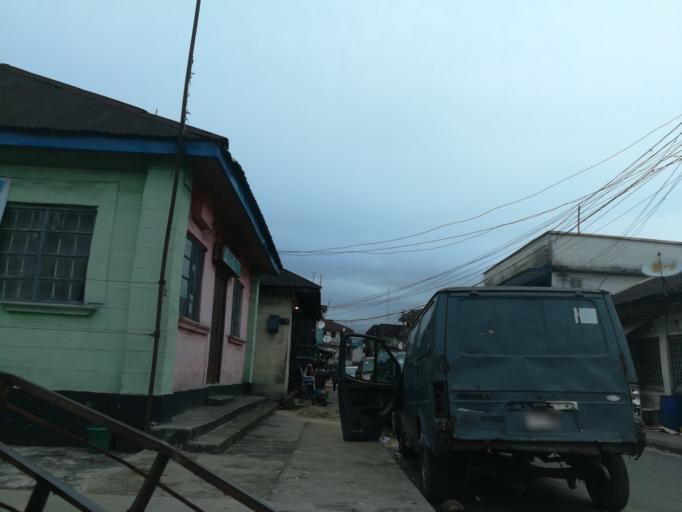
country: NG
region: Rivers
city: Port Harcourt
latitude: 4.7641
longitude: 7.0207
